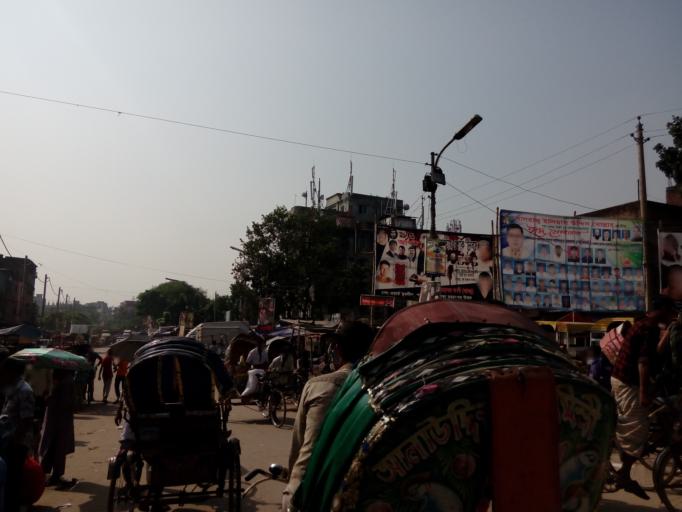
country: BD
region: Dhaka
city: Tungi
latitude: 23.8189
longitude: 90.3780
